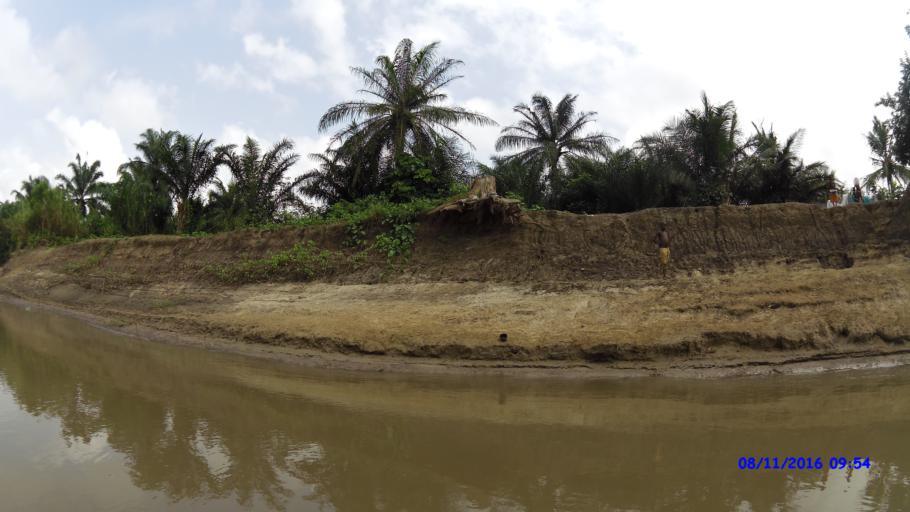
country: BJ
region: Mono
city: Come
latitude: 6.4397
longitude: 1.7645
